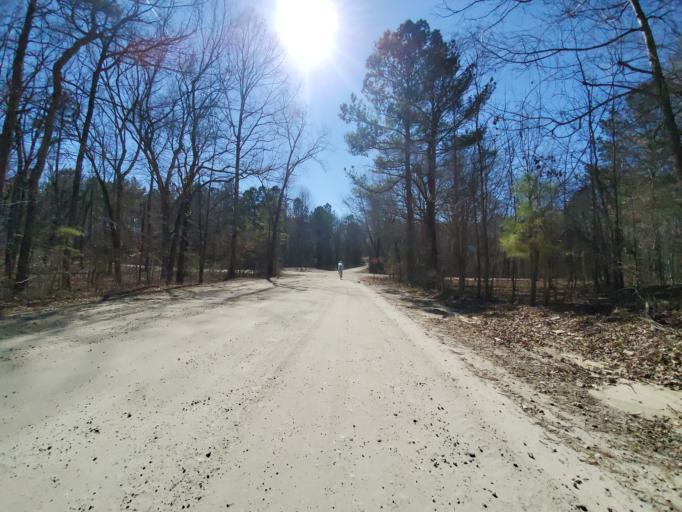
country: US
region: Georgia
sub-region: Gwinnett County
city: Dacula
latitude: 33.9770
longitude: -83.8552
